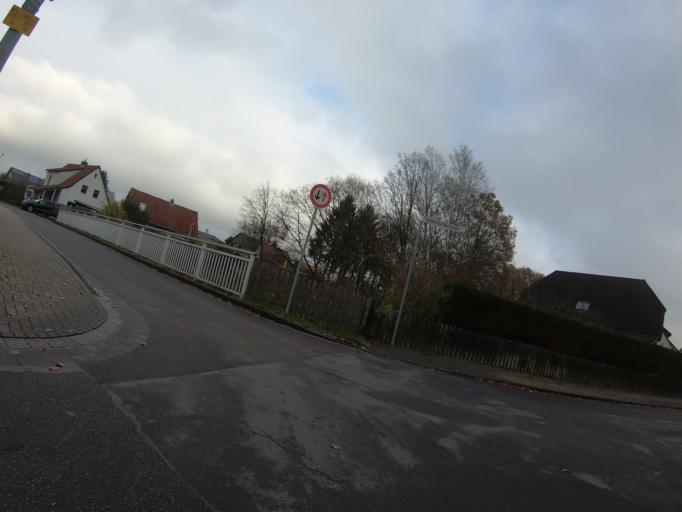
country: DE
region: Lower Saxony
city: Wagenhoff
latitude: 52.5152
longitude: 10.5341
